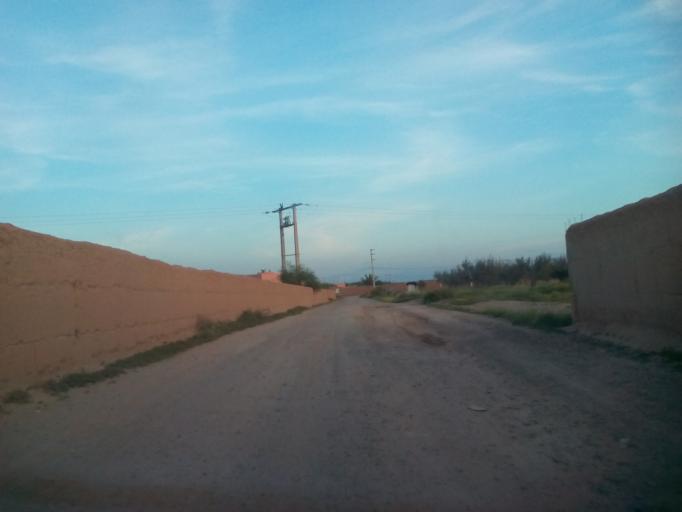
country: MA
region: Marrakech-Tensift-Al Haouz
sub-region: Marrakech
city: Marrakesh
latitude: 31.6261
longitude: -8.2849
